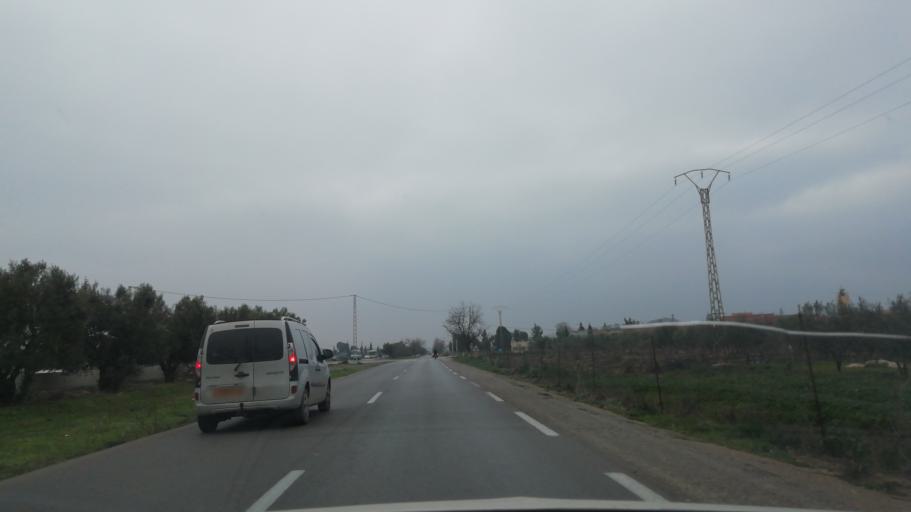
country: DZ
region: Sidi Bel Abbes
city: Sfizef
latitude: 35.2189
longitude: -0.2990
